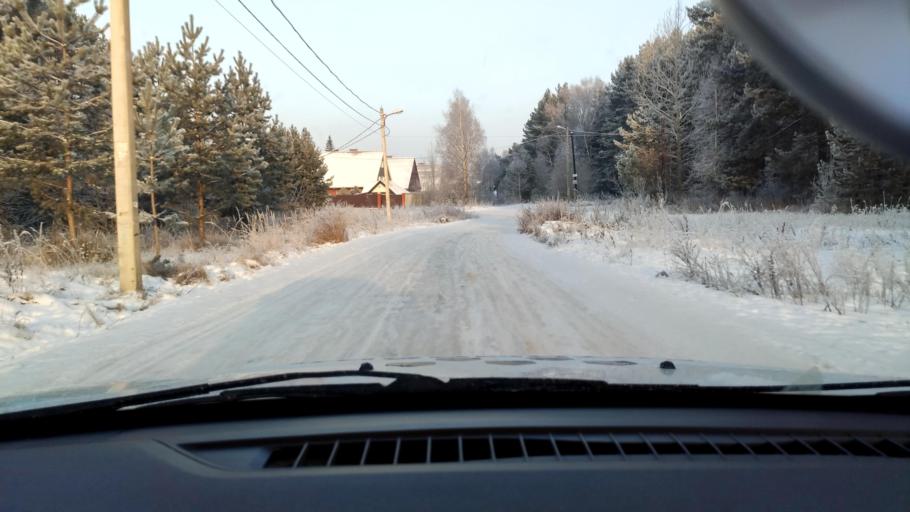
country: RU
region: Perm
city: Kondratovo
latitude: 58.0491
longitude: 56.1029
